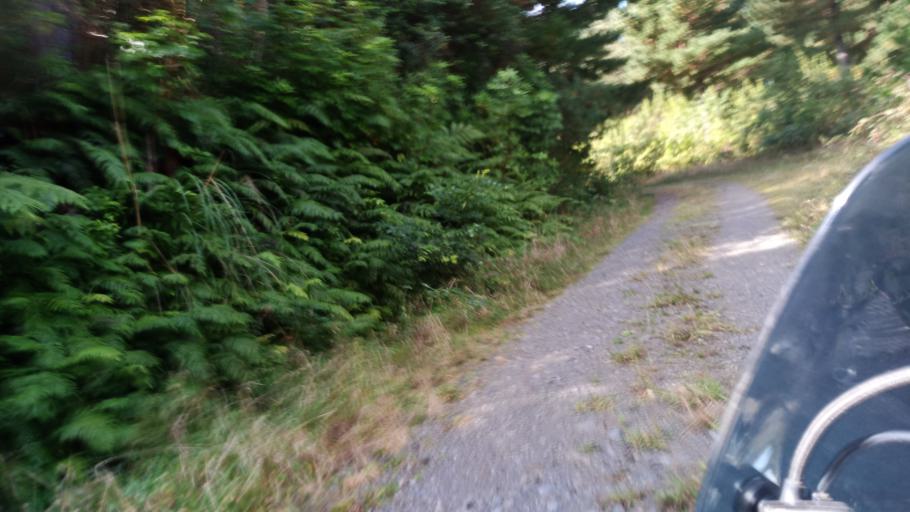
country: NZ
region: Hawke's Bay
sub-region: Wairoa District
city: Wairoa
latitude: -39.0035
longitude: 177.0843
